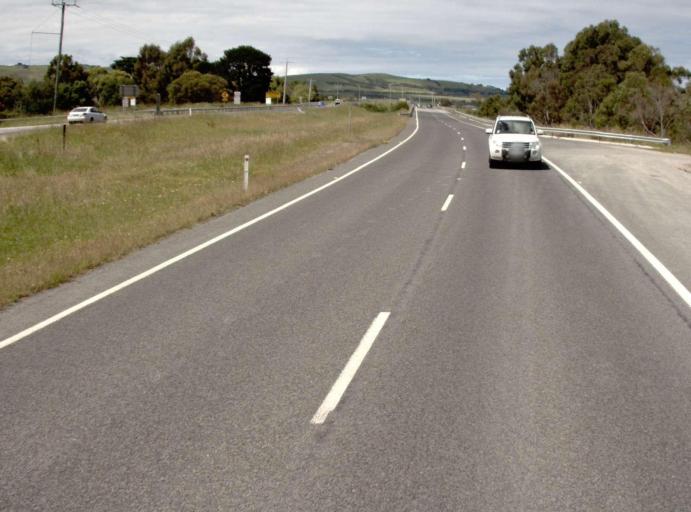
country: AU
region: Victoria
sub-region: Bass Coast
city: North Wonthaggi
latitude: -38.4839
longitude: 145.4646
